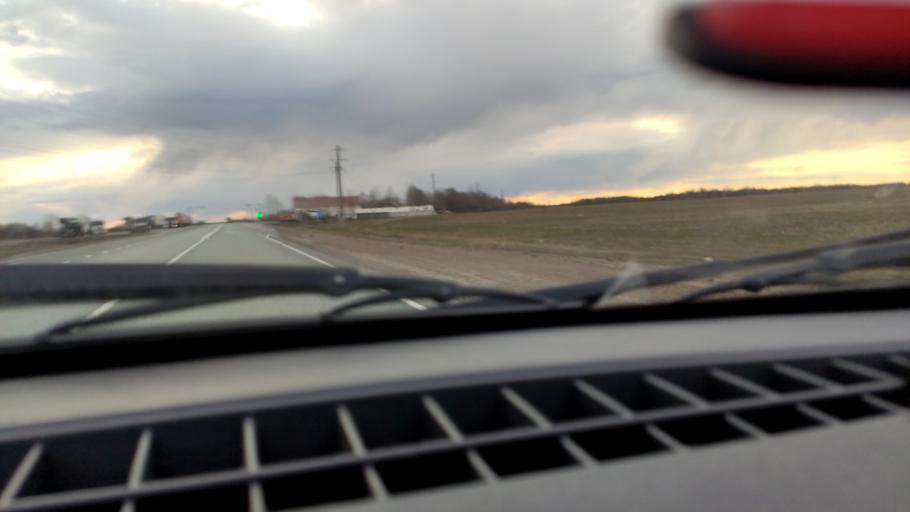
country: RU
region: Bashkortostan
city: Kudeyevskiy
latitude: 54.8168
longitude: 56.7408
